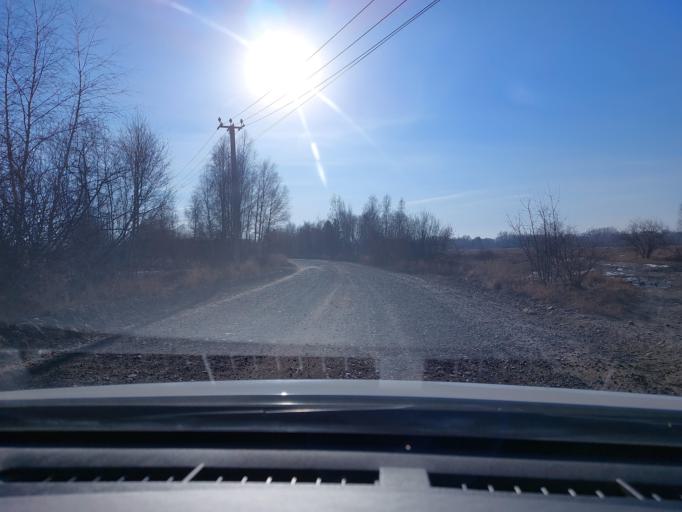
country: RU
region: Irkutsk
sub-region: Irkutskiy Rayon
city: Irkutsk
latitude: 52.3085
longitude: 104.2724
